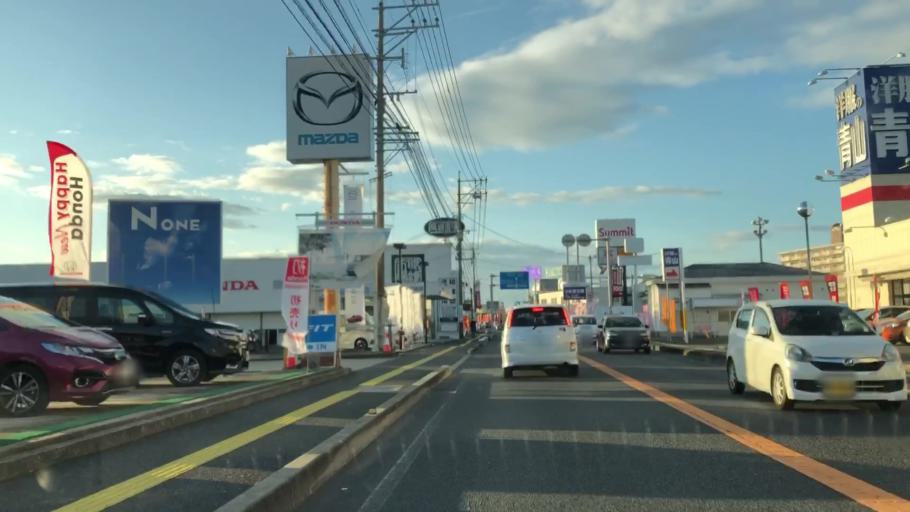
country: JP
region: Oita
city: Bungo-Takada-shi
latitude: 33.5335
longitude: 131.3305
